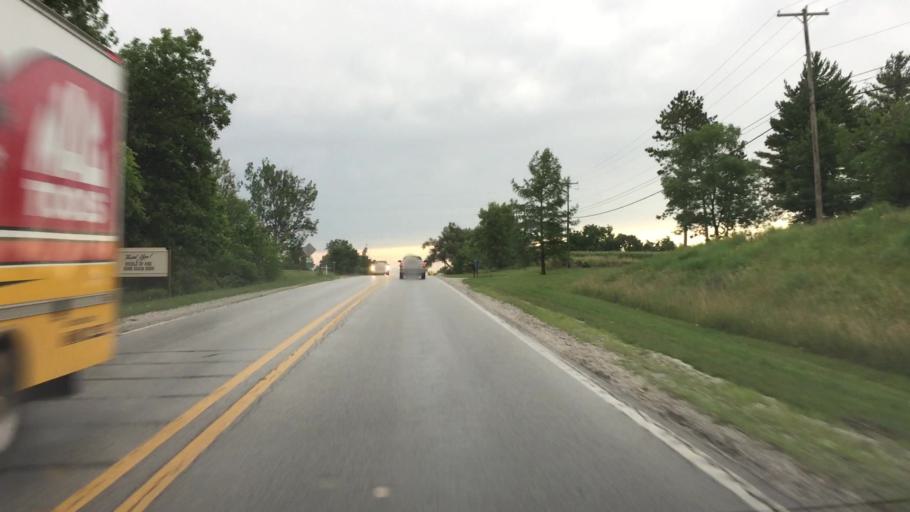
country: US
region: Illinois
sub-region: Hancock County
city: Hamilton
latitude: 40.3830
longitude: -91.3411
